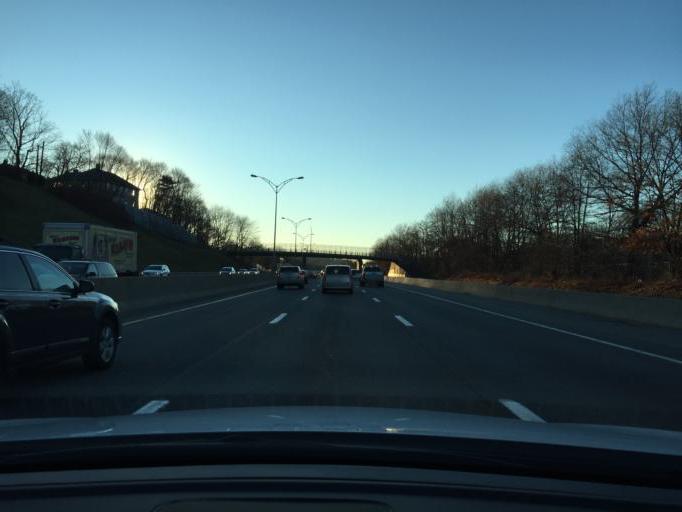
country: US
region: Massachusetts
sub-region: Middlesex County
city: Watertown
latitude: 42.3546
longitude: -71.1945
